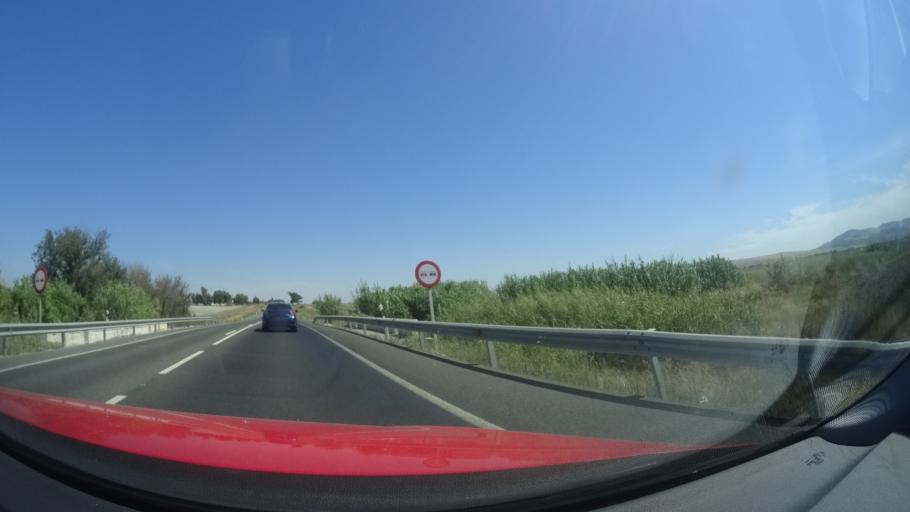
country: ES
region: Andalusia
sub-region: Provincia de Sevilla
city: Lebrija
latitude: 36.8943
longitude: -6.0007
